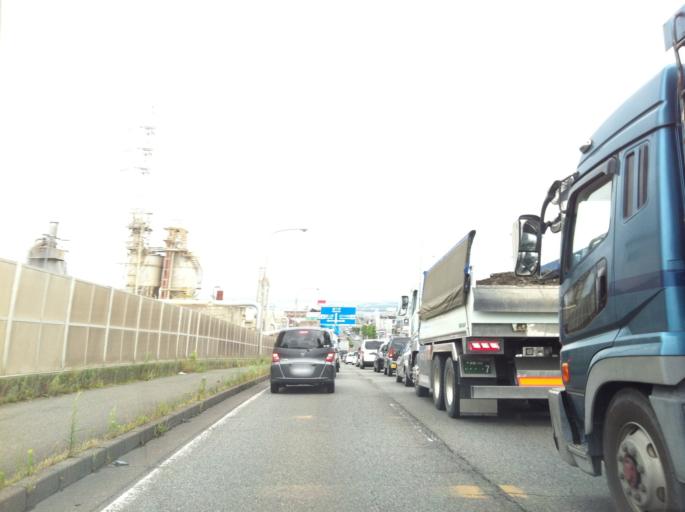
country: JP
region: Shizuoka
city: Fuji
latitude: 35.1506
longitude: 138.6639
